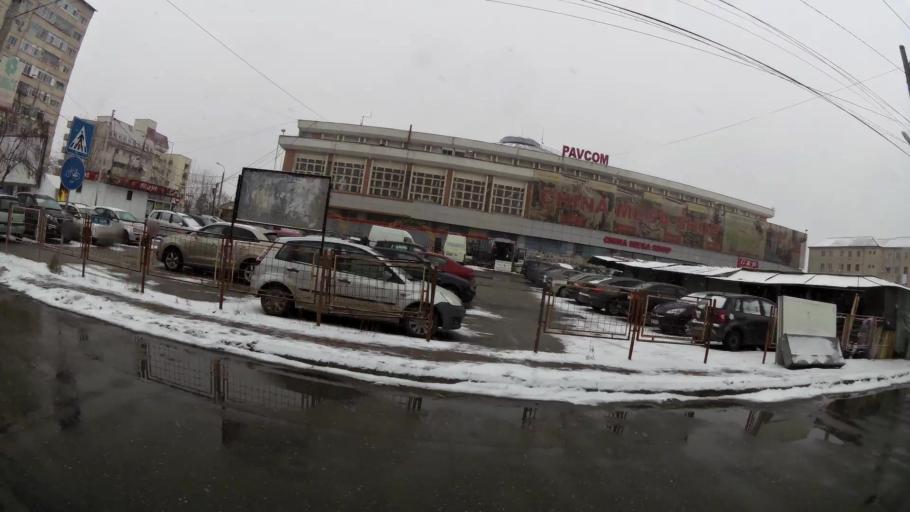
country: RO
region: Dambovita
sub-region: Municipiul Targoviste
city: Targoviste
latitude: 44.9199
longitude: 25.4505
